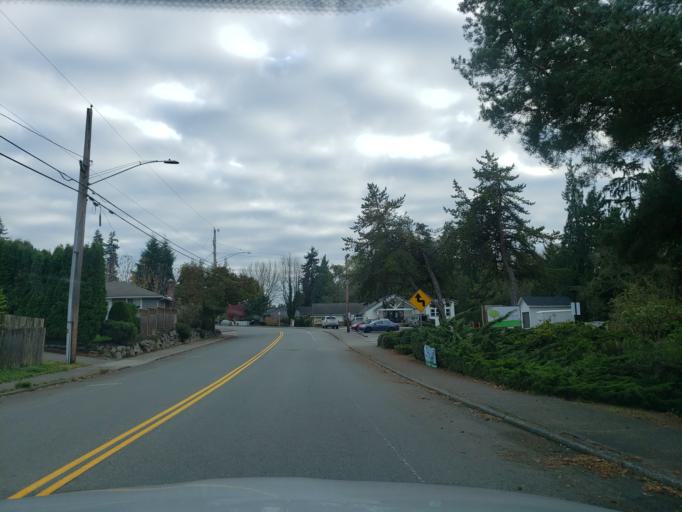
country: US
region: Washington
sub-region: Snohomish County
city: Everett
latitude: 47.9299
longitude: -122.2285
